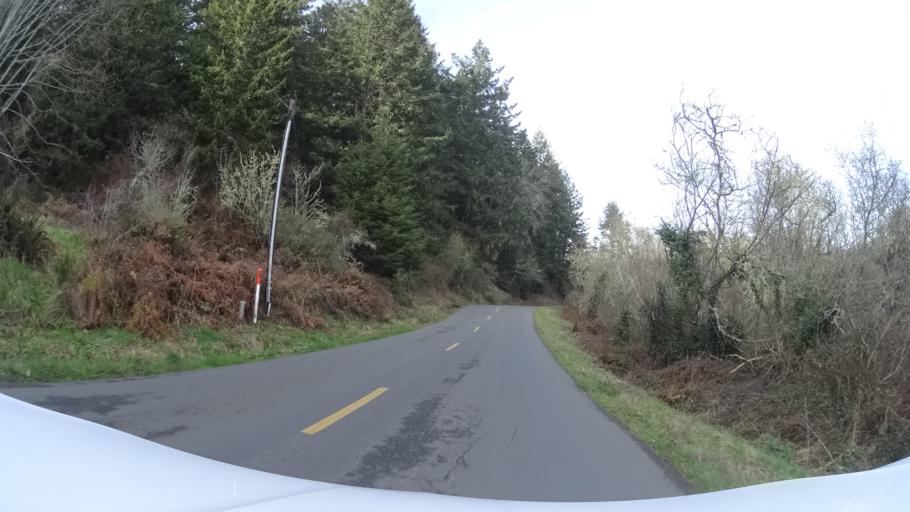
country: US
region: California
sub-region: Humboldt County
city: Ferndale
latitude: 40.5683
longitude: -124.2706
